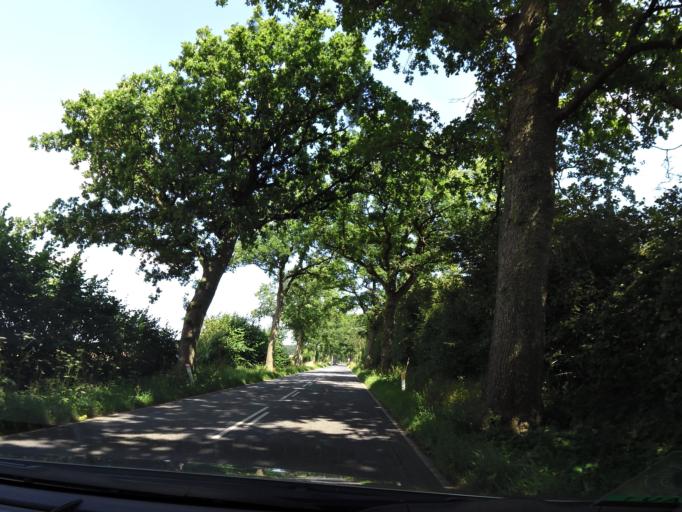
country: DK
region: South Denmark
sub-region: Assens Kommune
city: Arup
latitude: 55.3990
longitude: 10.0448
